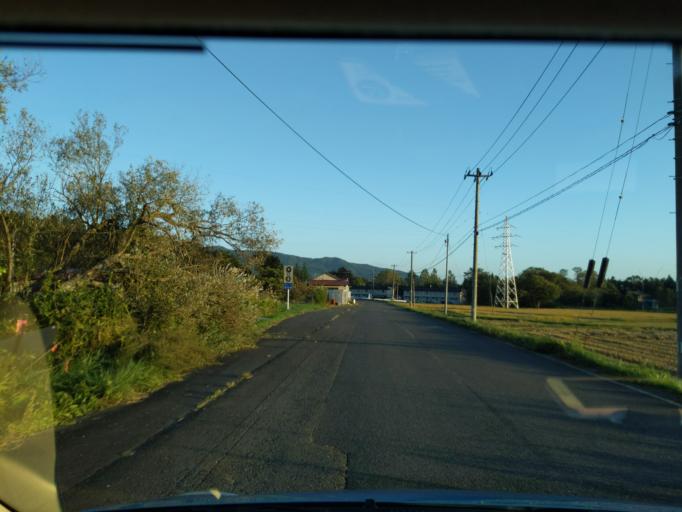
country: JP
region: Iwate
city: Mizusawa
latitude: 39.0532
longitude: 141.1169
